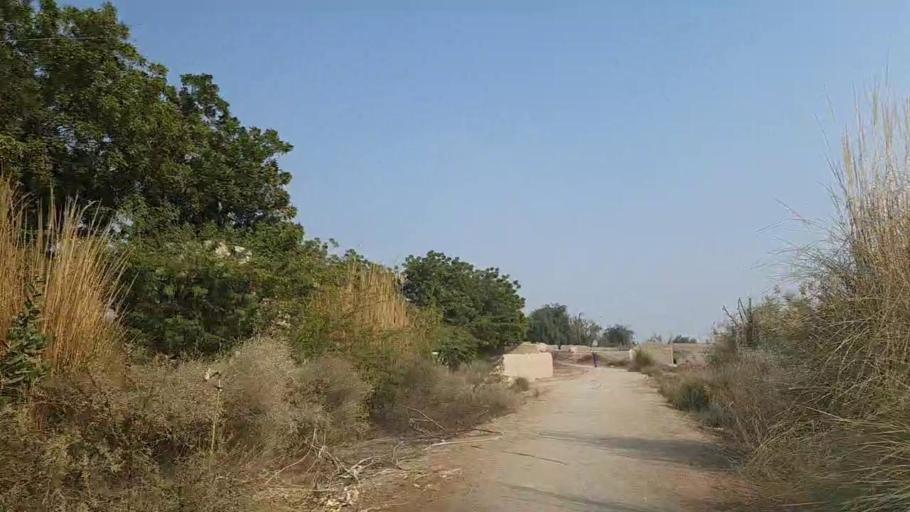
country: PK
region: Sindh
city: Daur
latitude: 26.5079
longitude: 68.4364
